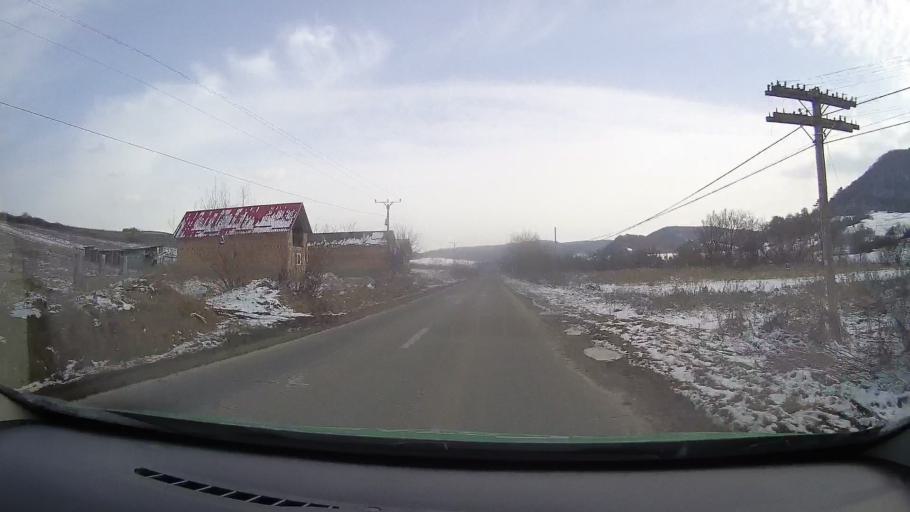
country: RO
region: Mures
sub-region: Comuna Apold
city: Saes
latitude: 46.1466
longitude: 24.7763
